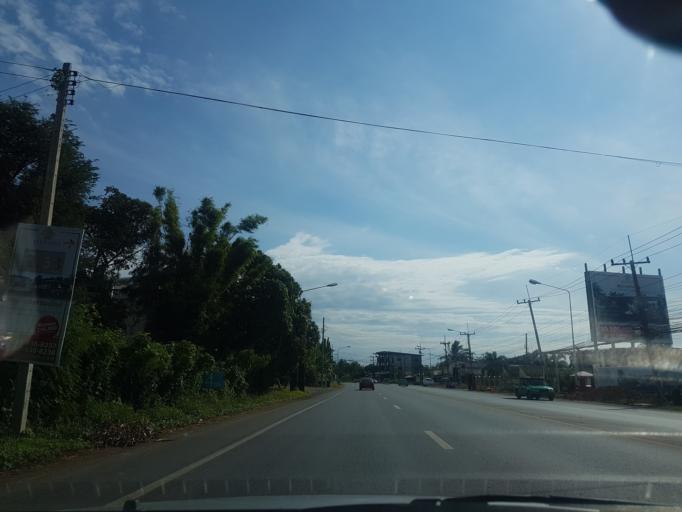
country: TH
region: Lop Buri
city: Lop Buri
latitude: 14.8002
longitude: 100.7244
